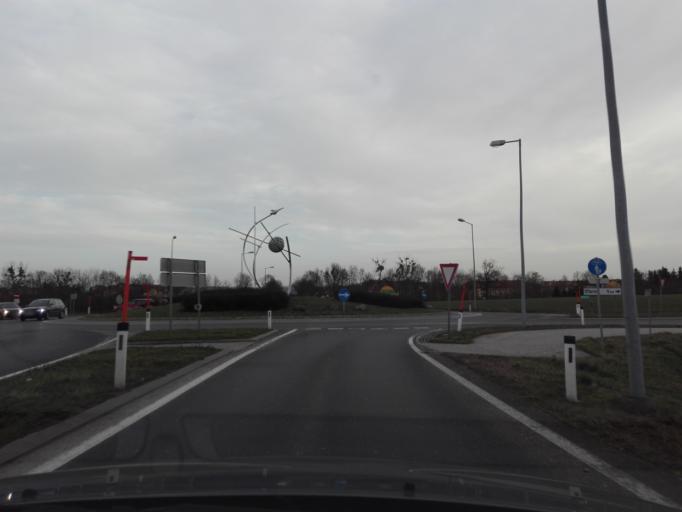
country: AT
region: Upper Austria
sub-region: Politischer Bezirk Linz-Land
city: Horsching
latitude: 48.2274
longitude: 14.1657
